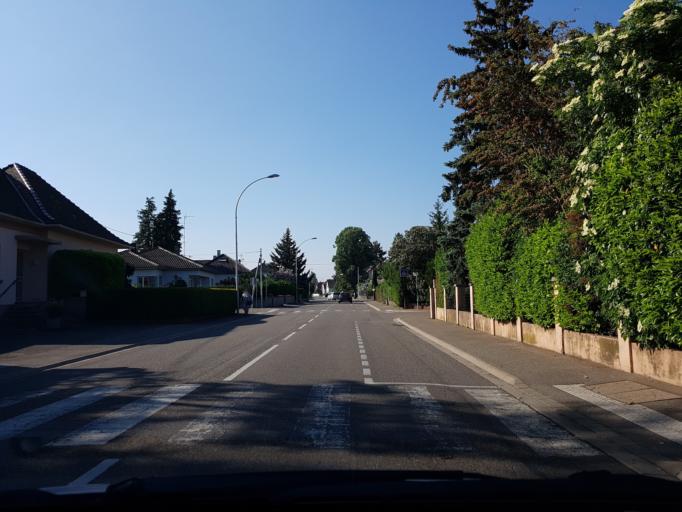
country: FR
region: Alsace
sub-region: Departement du Haut-Rhin
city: Rixheim
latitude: 47.7471
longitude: 7.3989
